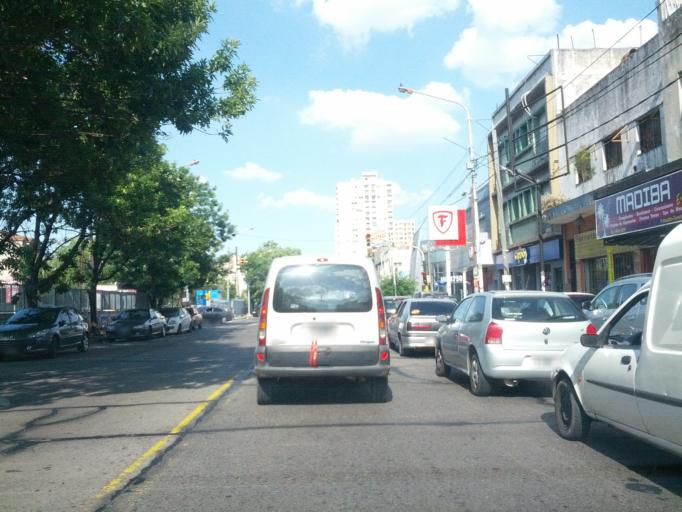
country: AR
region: Buenos Aires
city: San Justo
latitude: -34.6421
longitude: -58.5738
